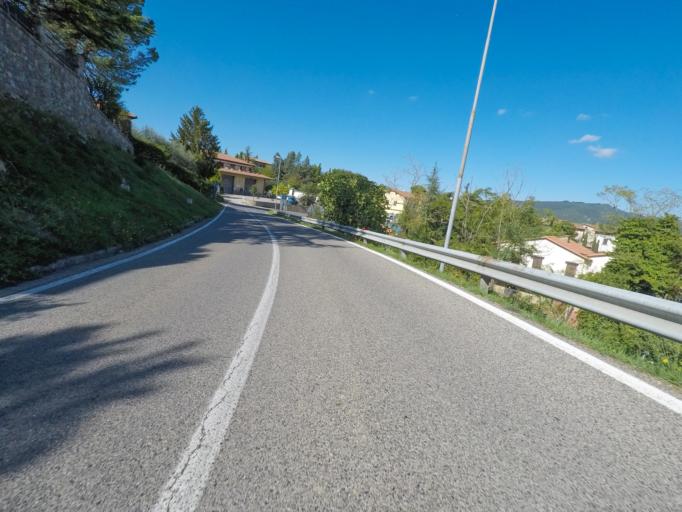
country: IT
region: Tuscany
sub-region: Provincia di Siena
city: Radda in Chianti
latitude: 43.4834
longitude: 11.3659
